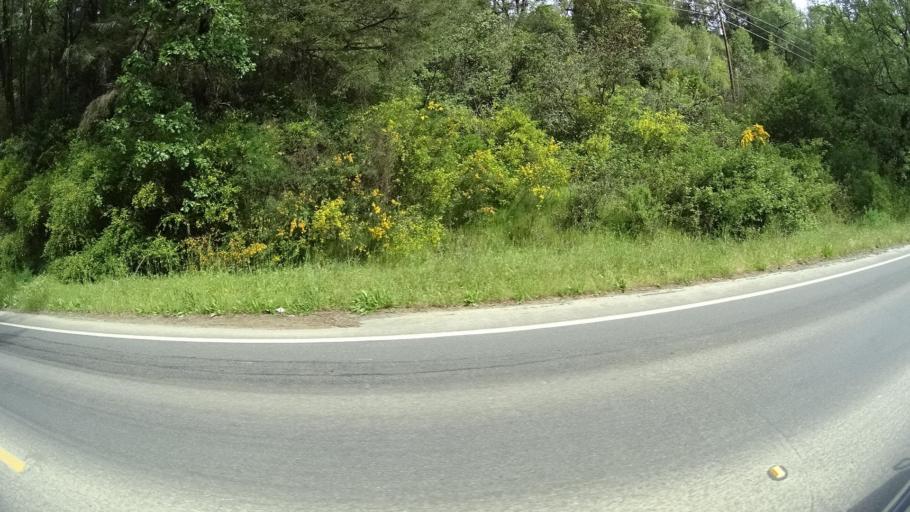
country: US
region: California
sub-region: Humboldt County
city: Redway
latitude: 40.1157
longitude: -123.8085
